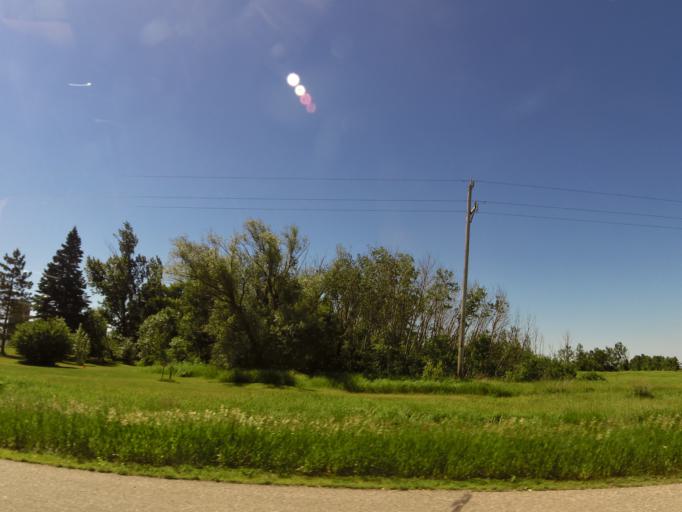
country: US
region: Minnesota
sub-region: Polk County
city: Crookston
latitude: 47.7604
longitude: -96.4364
